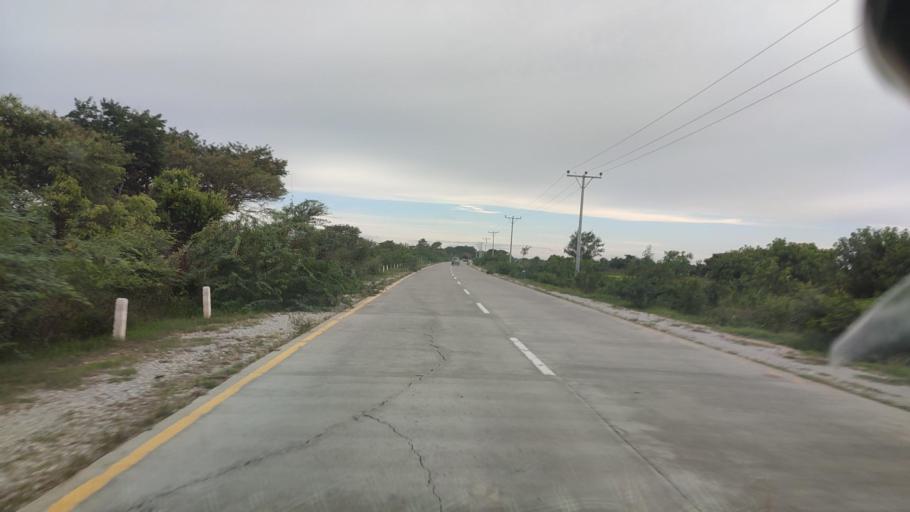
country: MM
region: Mandalay
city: Kyaukse
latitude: 21.3200
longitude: 96.0236
